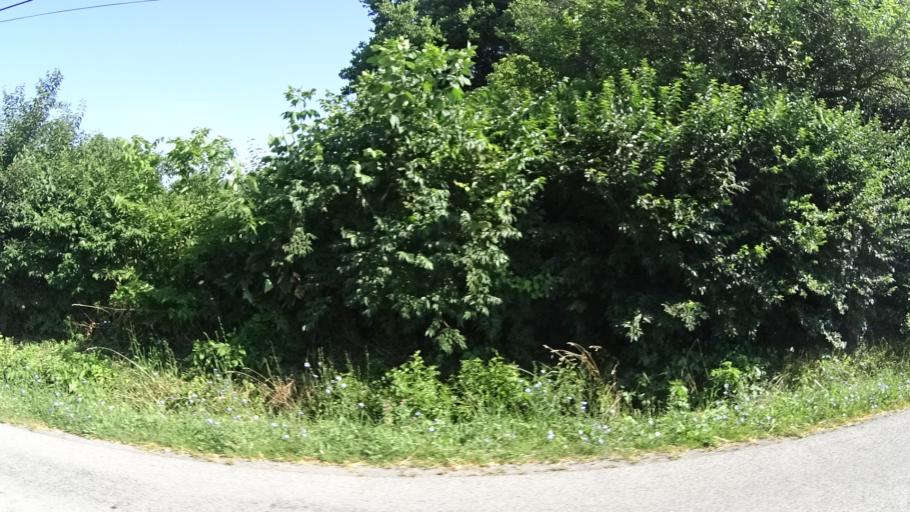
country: US
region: Ohio
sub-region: Huron County
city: Bellevue
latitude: 41.3746
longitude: -82.8075
